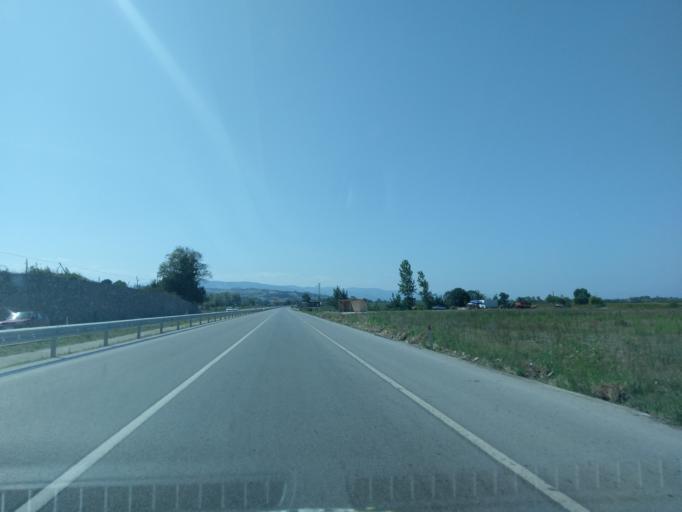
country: TR
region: Samsun
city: Alacam
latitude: 41.6084
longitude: 35.6723
